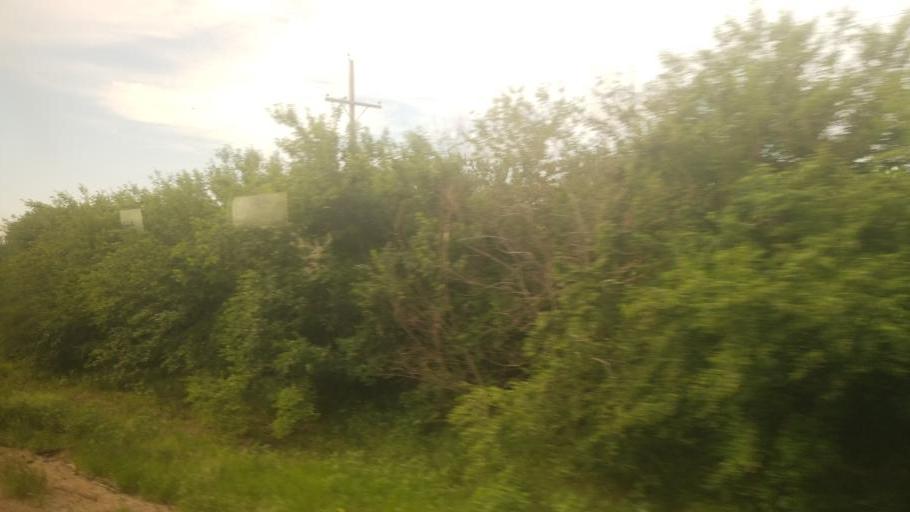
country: US
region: Kansas
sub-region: Douglas County
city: Lawrence
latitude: 38.9537
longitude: -95.1929
